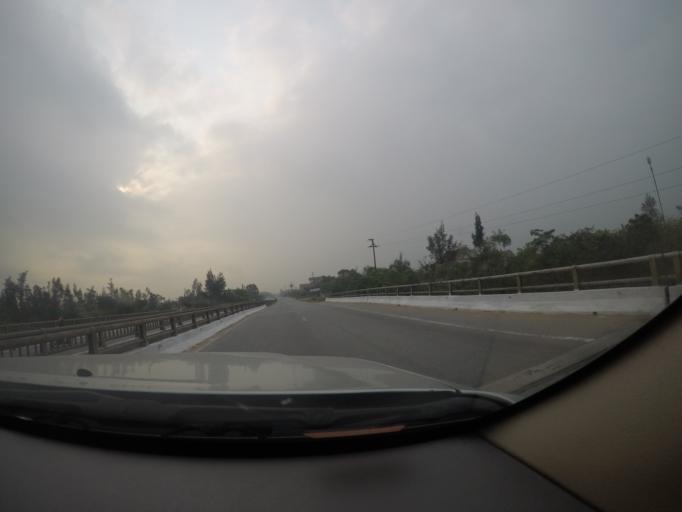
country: VN
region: Ha Tinh
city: Cam Xuyen
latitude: 18.2413
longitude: 106.0142
